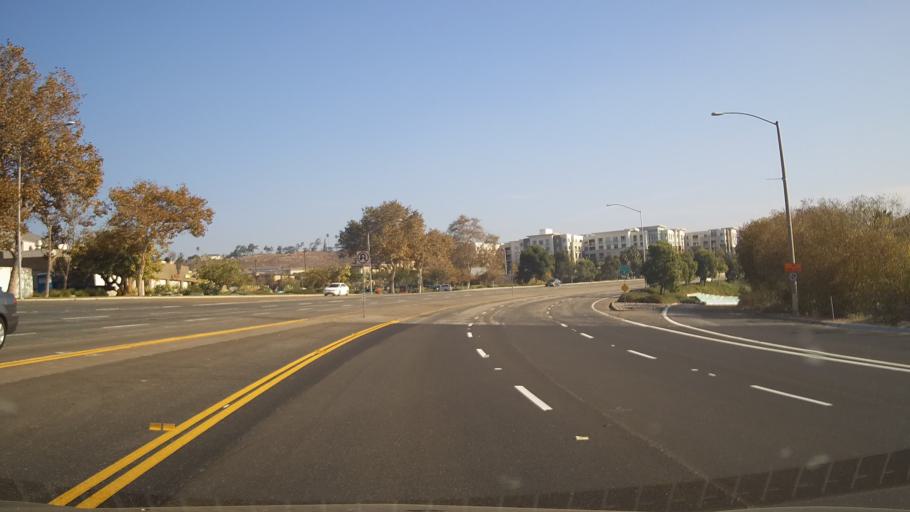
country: US
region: California
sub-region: San Diego County
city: San Diego
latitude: 32.7738
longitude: -117.1563
